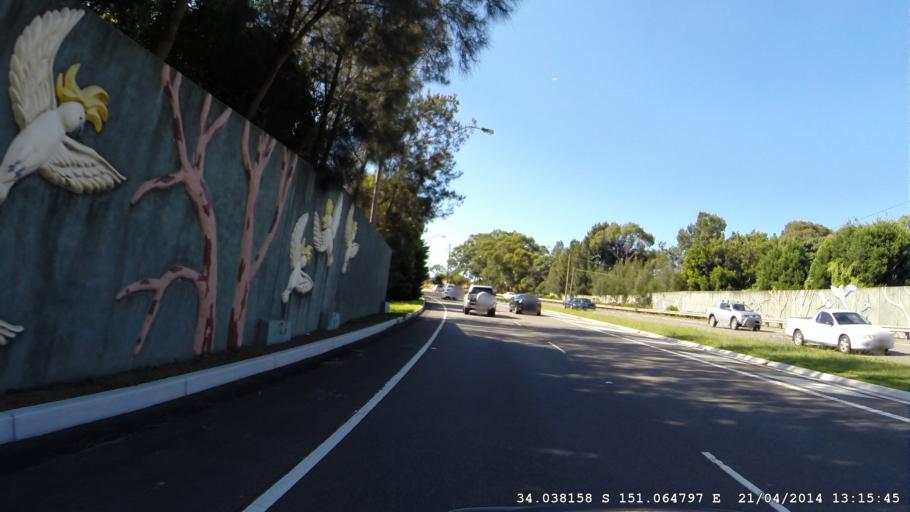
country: AU
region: New South Wales
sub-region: Sutherland Shire
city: Kirrawee
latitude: -34.0382
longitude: 151.0648
